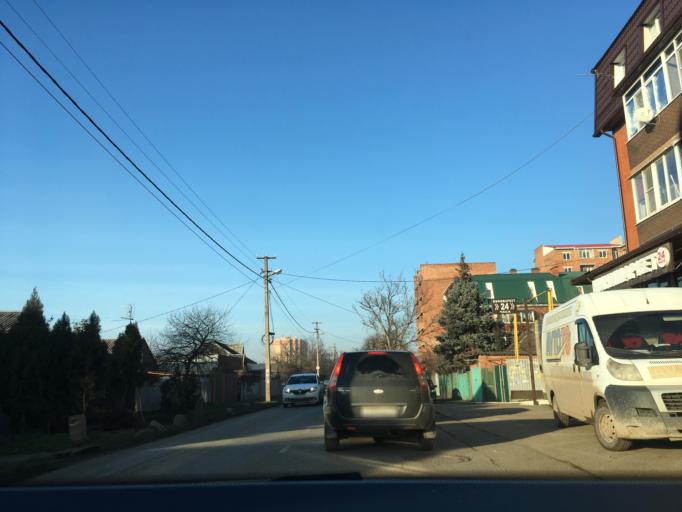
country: RU
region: Krasnodarskiy
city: Krasnodar
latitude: 45.0794
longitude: 39.0207
